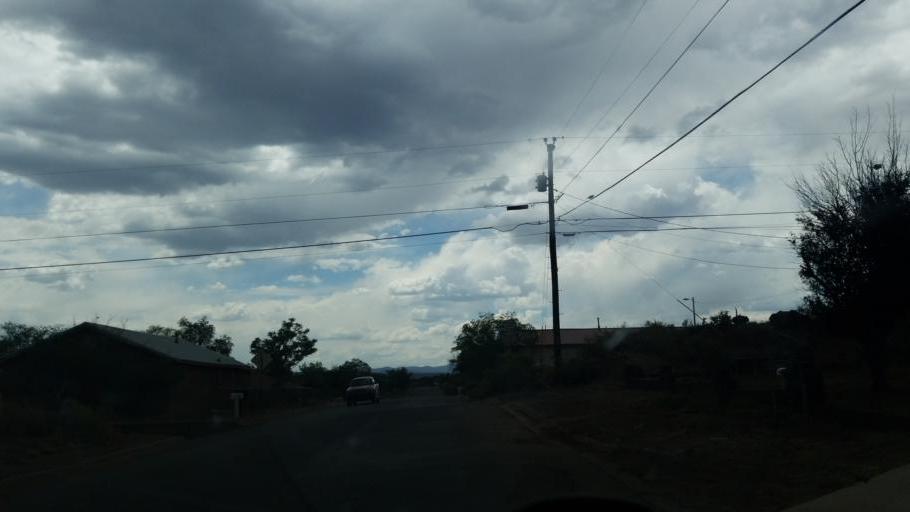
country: US
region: New Mexico
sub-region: Cibola County
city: Grants
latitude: 35.1573
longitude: -107.8544
